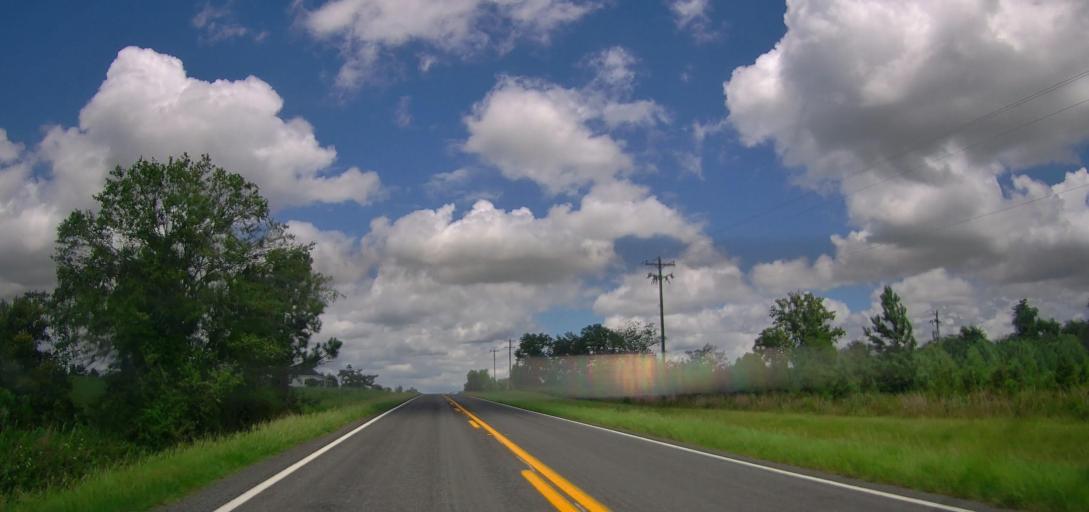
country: US
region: Georgia
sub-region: Turner County
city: Ashburn
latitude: 31.8028
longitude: -83.5769
